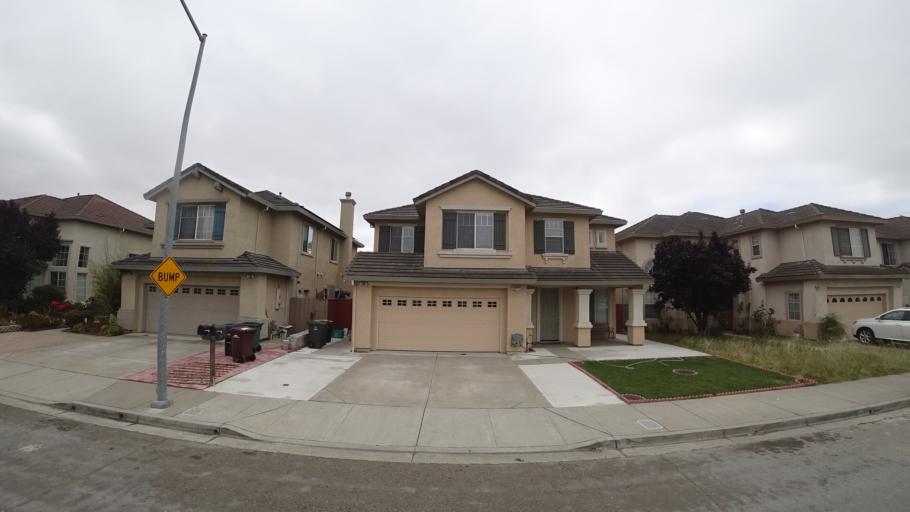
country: US
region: California
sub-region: Alameda County
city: Hayward
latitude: 37.6305
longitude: -122.0677
